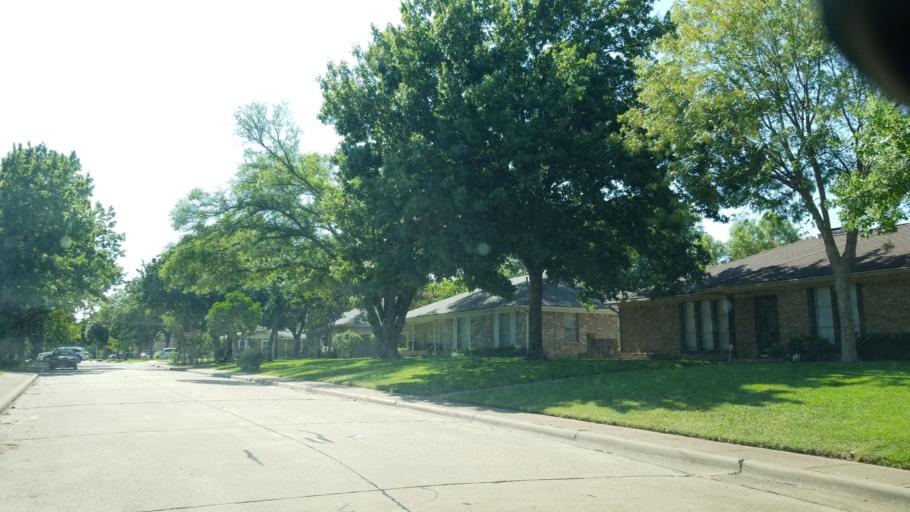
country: US
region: Texas
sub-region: Dallas County
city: Farmers Branch
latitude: 32.9195
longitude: -96.8866
